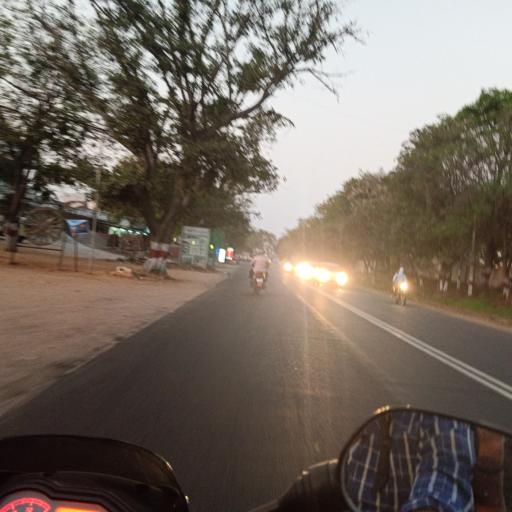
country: IN
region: Telangana
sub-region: Rangareddi
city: Secunderabad
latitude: 17.5458
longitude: 78.5345
